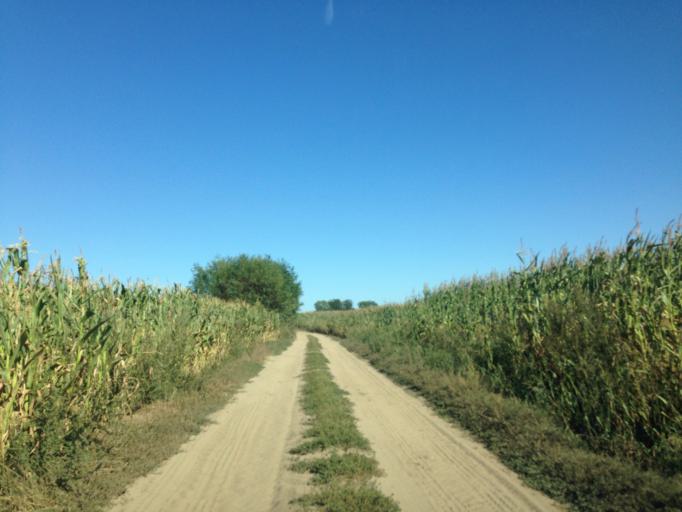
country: PL
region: Kujawsko-Pomorskie
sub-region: Powiat brodnicki
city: Brodnica
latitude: 53.2114
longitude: 19.4104
